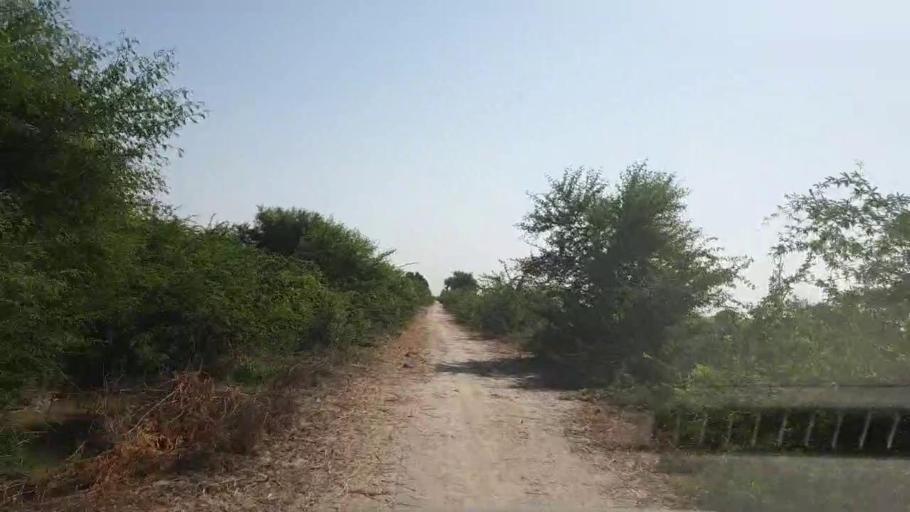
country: PK
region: Sindh
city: Kadhan
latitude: 24.6226
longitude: 68.9956
